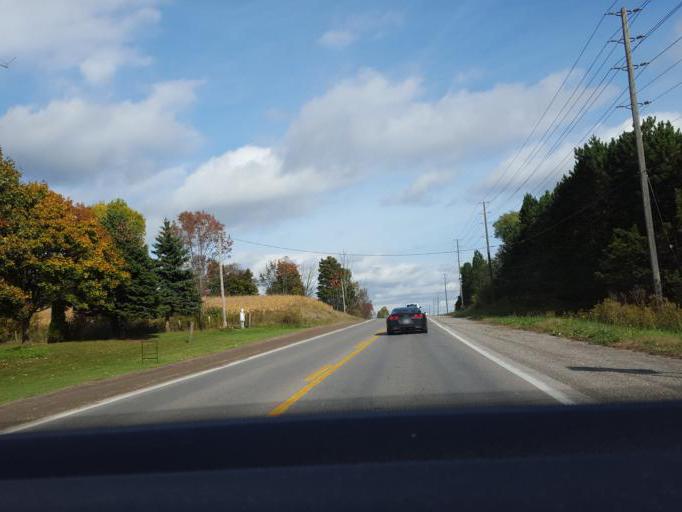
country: CA
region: Ontario
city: Oshawa
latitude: 43.9576
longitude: -78.7711
